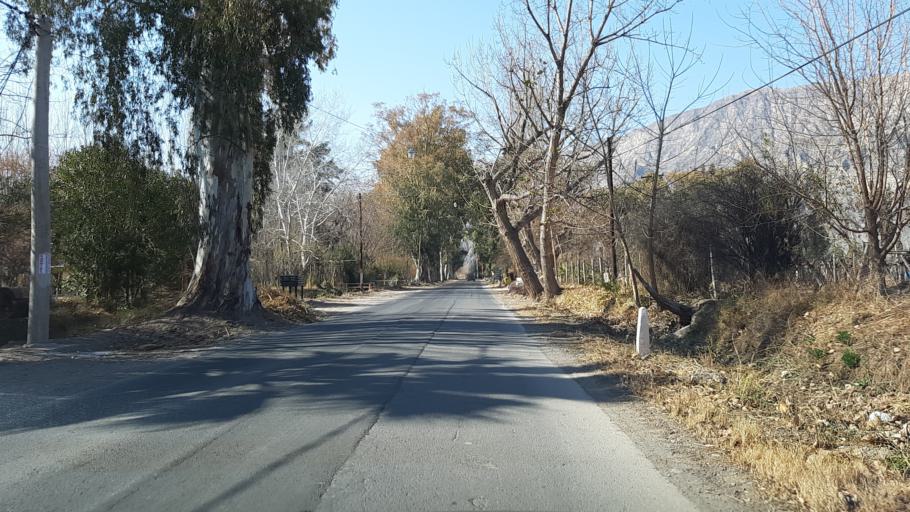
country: AR
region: San Juan
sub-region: Departamento de Zonda
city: Zonda
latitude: -31.5610
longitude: -68.7244
